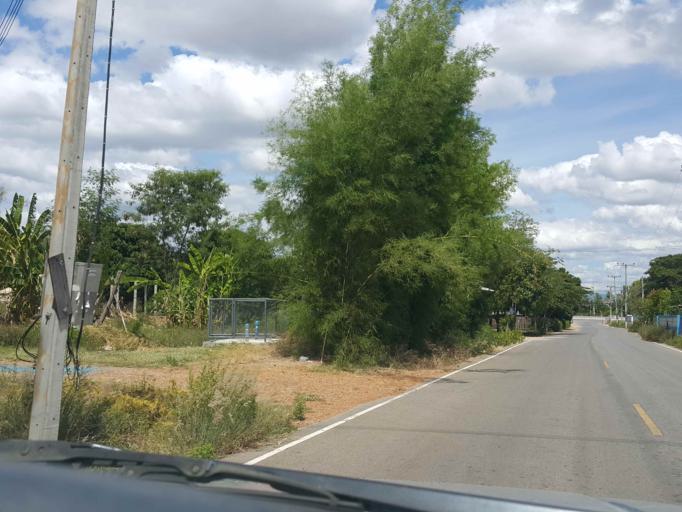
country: TH
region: Chiang Mai
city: Doi Lo
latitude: 18.4562
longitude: 98.7687
